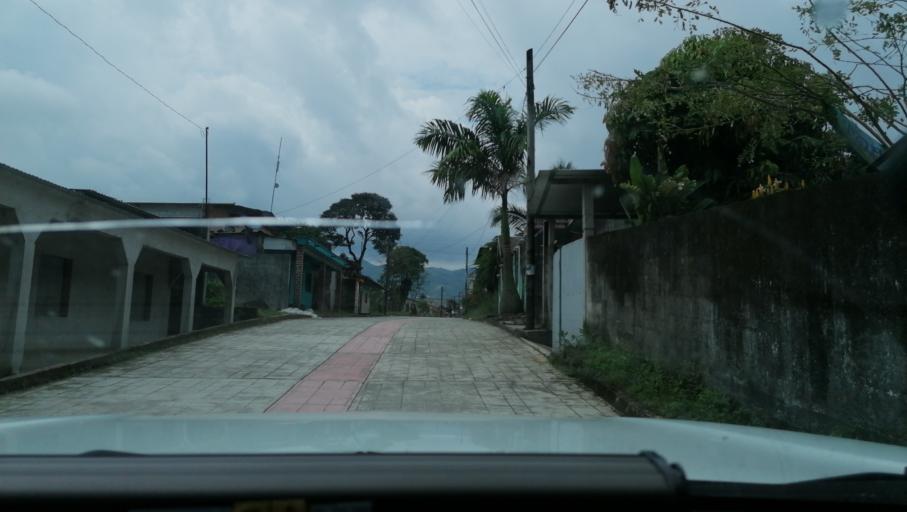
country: MX
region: Chiapas
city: Ixtacomitan
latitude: 17.3378
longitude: -93.1295
